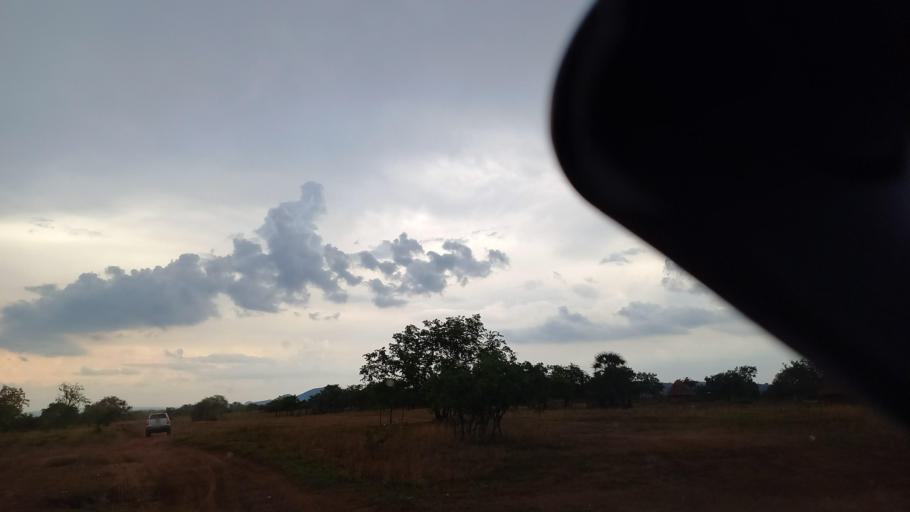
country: ZM
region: Lusaka
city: Kafue
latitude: -15.9744
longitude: 28.2524
